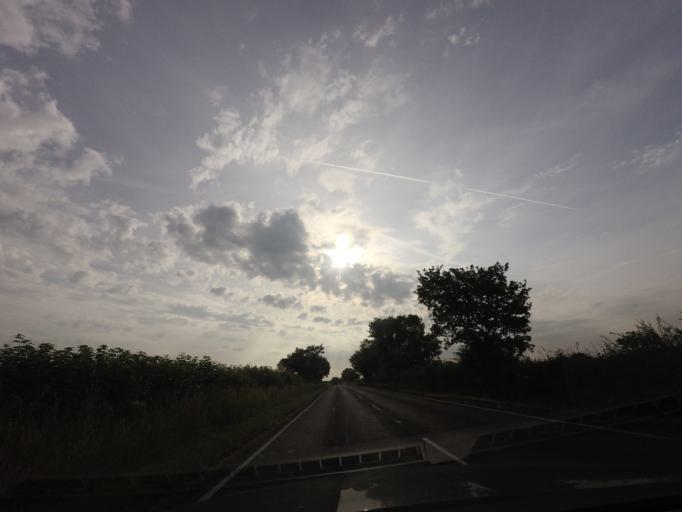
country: GB
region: England
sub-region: Staffordshire
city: Wheaton Aston
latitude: 52.6941
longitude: -2.2138
